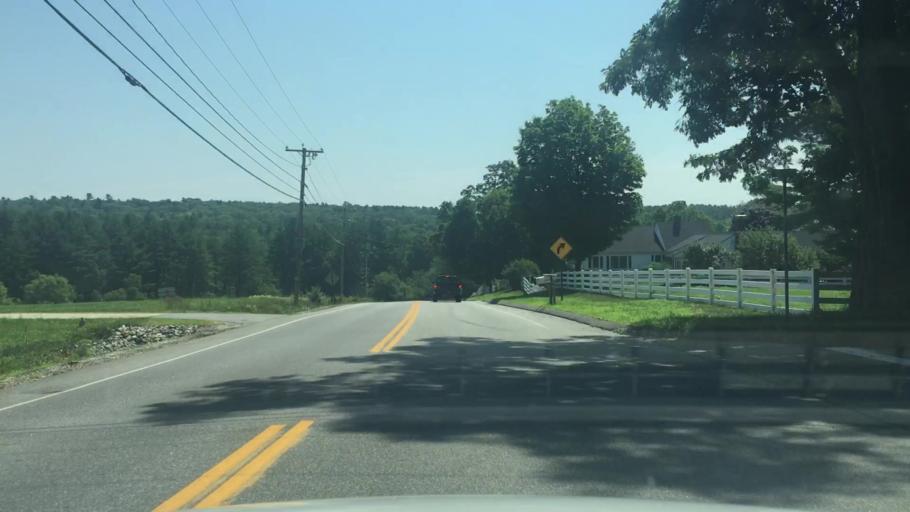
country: US
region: Maine
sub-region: Cumberland County
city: Cumberland Center
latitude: 43.8186
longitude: -70.2943
